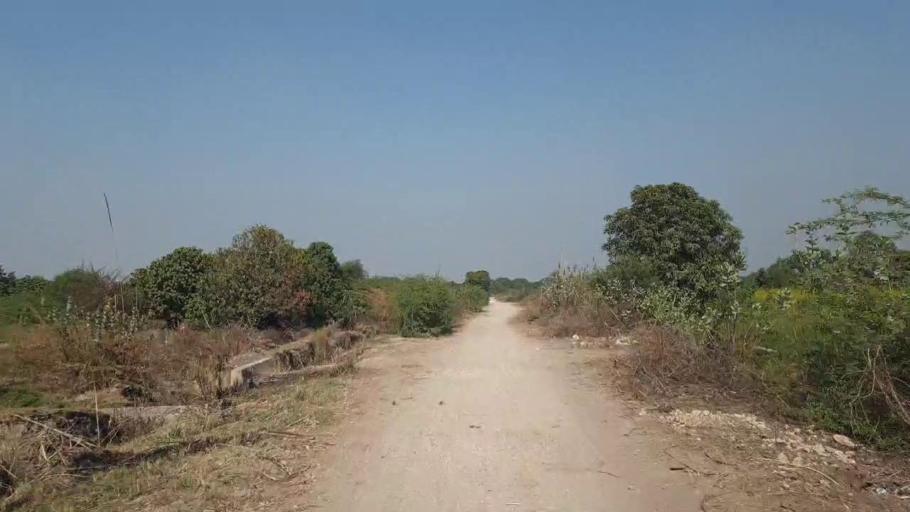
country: PK
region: Sindh
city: Chambar
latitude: 25.4122
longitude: 68.9069
